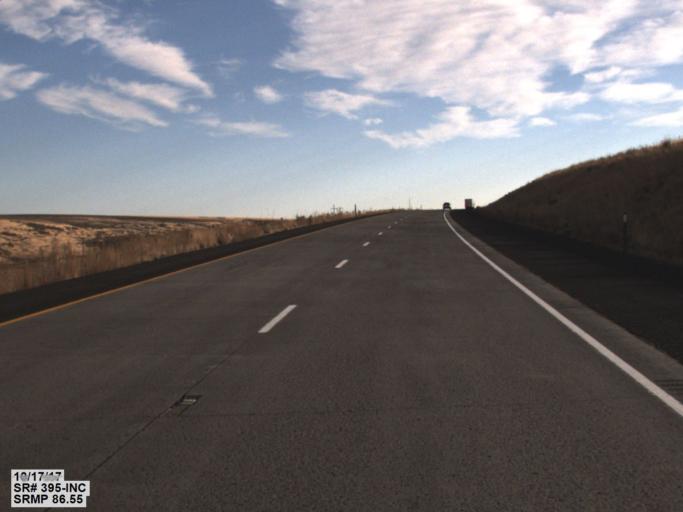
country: US
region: Washington
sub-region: Adams County
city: Ritzville
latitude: 47.0142
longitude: -118.5055
